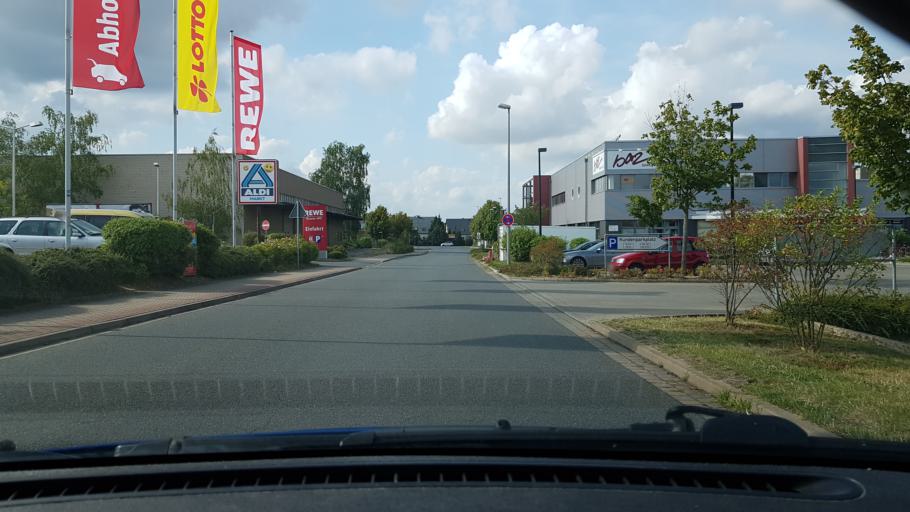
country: DE
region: Lower Saxony
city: Grossgoltern
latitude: 52.3038
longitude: 9.4884
